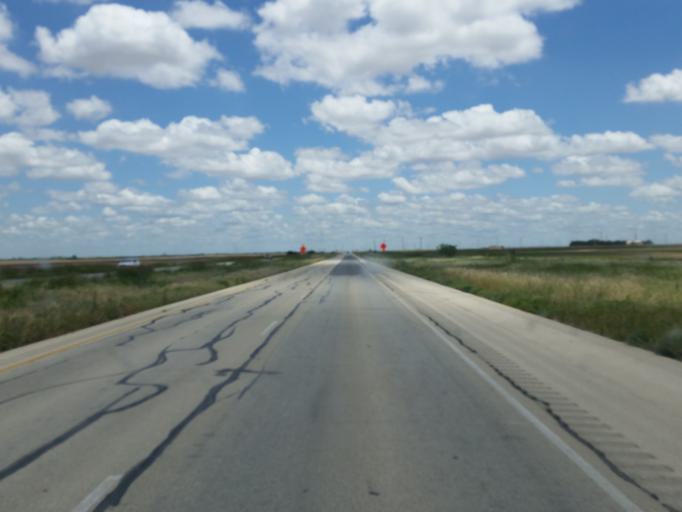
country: US
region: Texas
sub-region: Nolan County
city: Roscoe
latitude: 32.4847
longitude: -100.6248
